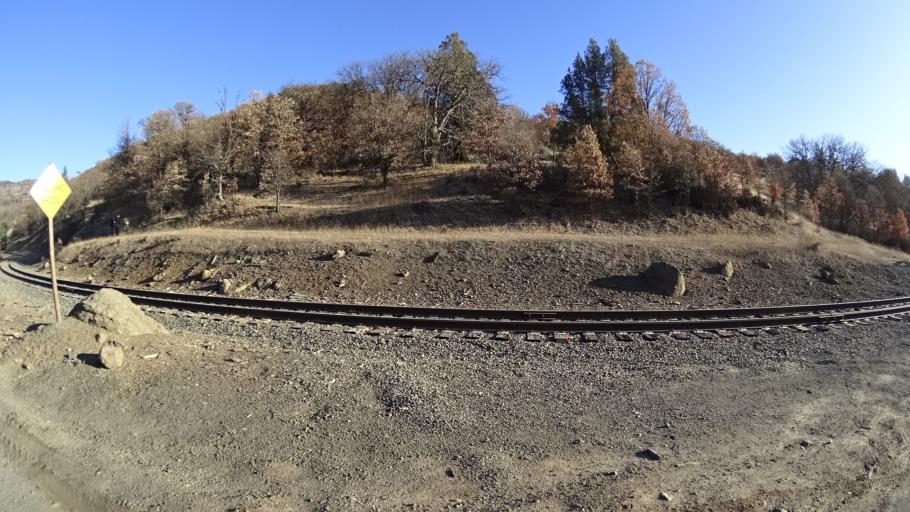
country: US
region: Oregon
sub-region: Jackson County
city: Ashland
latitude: 42.0046
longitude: -122.6450
